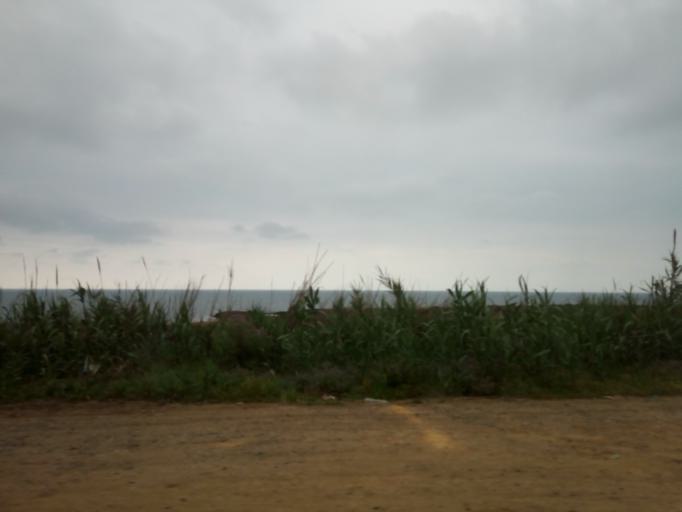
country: DZ
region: Tipaza
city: Tipasa
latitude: 36.5895
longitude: 2.4968
